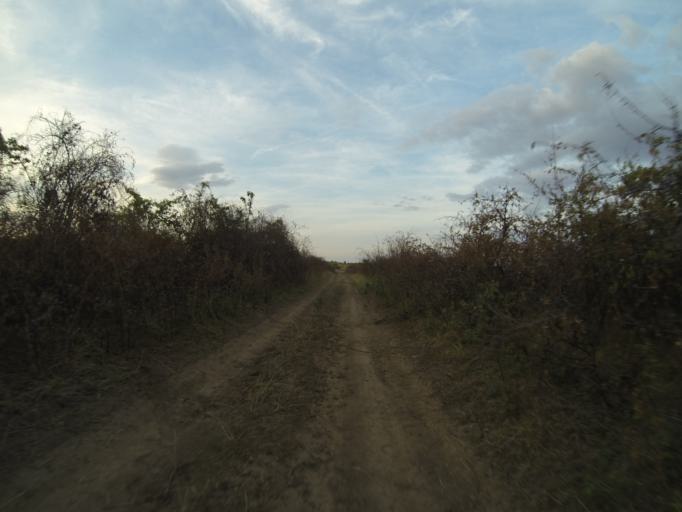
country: RO
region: Dolj
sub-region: Comuna Ceratu
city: Ceratu
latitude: 44.0988
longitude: 23.6767
